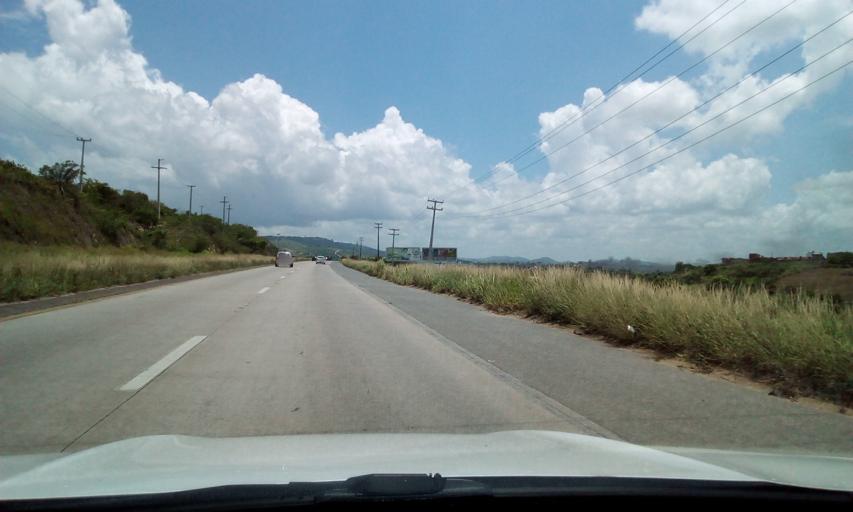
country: BR
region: Pernambuco
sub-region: Vitoria De Santo Antao
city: Vitoria de Santo Antao
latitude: -8.1350
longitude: -35.2918
